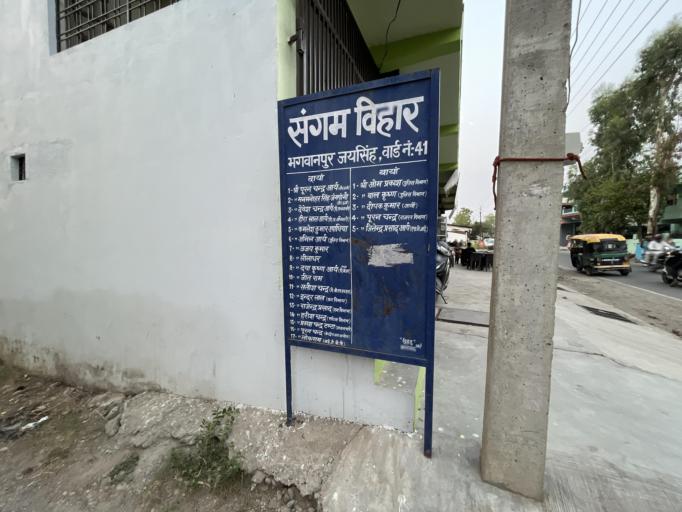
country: IN
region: Uttarakhand
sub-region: Naini Tal
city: Haldwani
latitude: 29.2235
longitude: 79.4801
